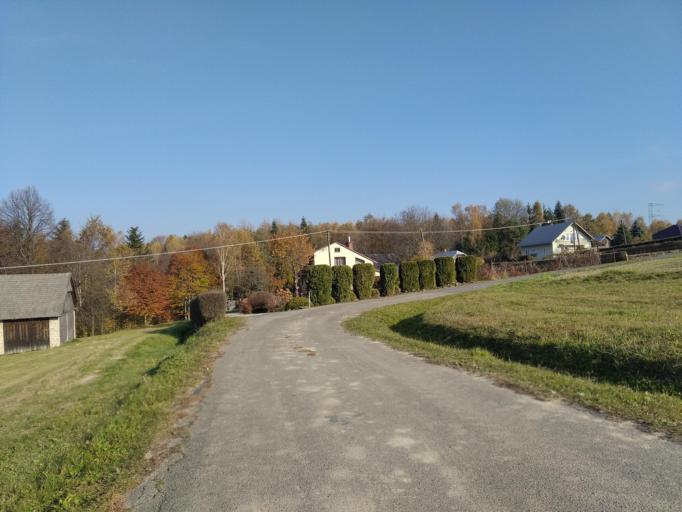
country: PL
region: Subcarpathian Voivodeship
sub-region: Powiat strzyzowski
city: Babica
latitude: 49.9022
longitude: 21.8460
